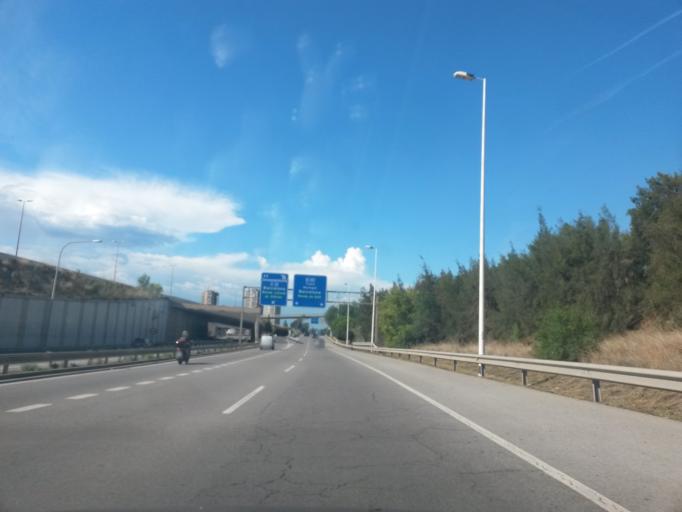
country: ES
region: Catalonia
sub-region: Provincia de Barcelona
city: Montgat
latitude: 41.4760
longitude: 2.2837
